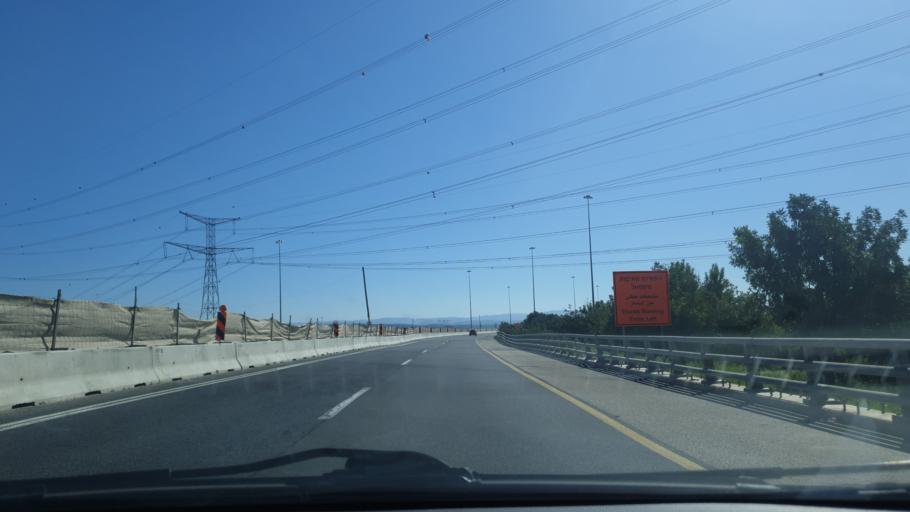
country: IL
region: Central District
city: Lod
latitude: 31.9103
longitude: 34.8983
